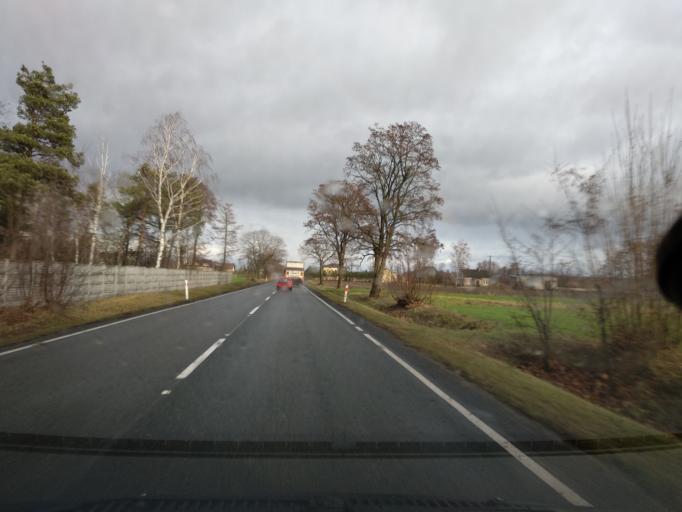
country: PL
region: Greater Poland Voivodeship
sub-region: Powiat koninski
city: Stare Miasto
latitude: 52.1337
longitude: 18.1841
